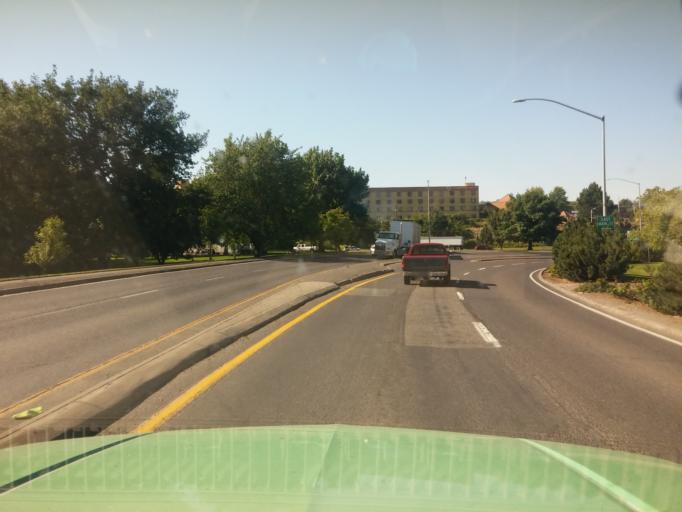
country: US
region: Idaho
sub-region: Nez Perce County
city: Lewiston
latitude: 46.4164
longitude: -117.0001
